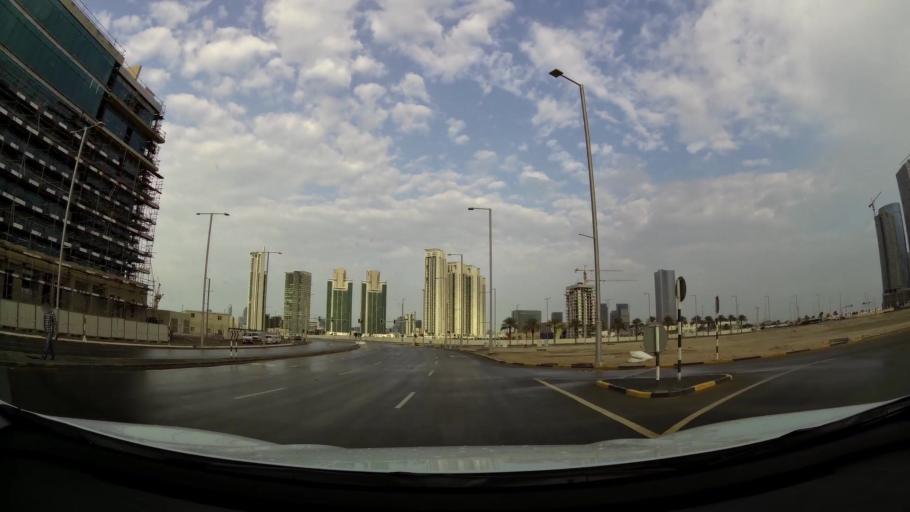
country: AE
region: Abu Dhabi
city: Abu Dhabi
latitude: 24.4872
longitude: 54.4041
